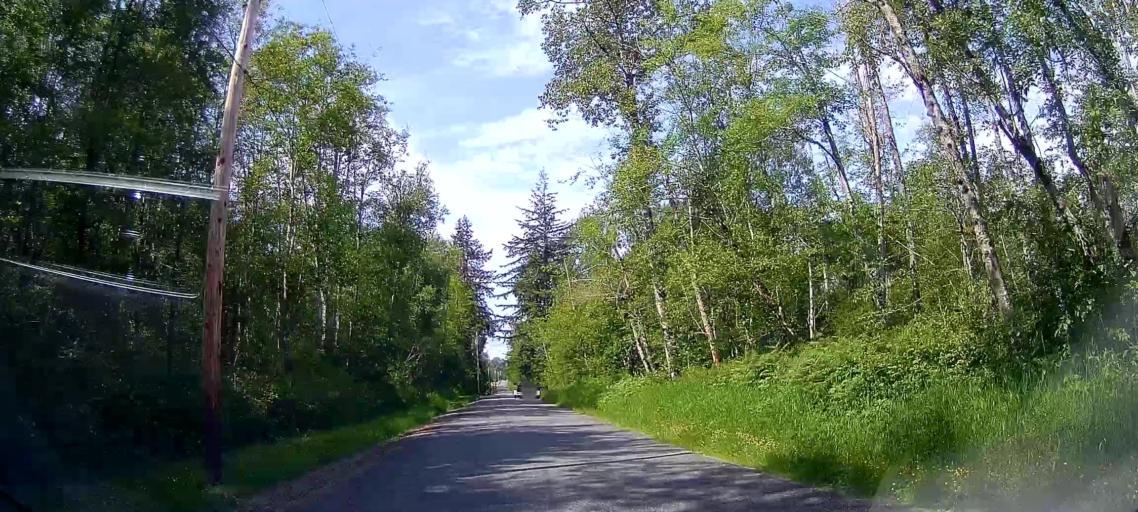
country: US
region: Washington
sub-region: Skagit County
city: Burlington
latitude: 48.5398
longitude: -122.3622
